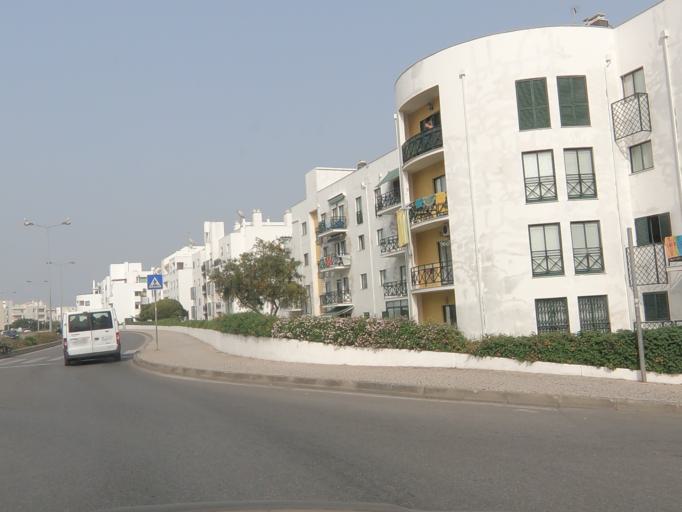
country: PT
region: Faro
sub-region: Silves
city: Armacao de Pera
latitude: 37.1048
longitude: -8.3583
